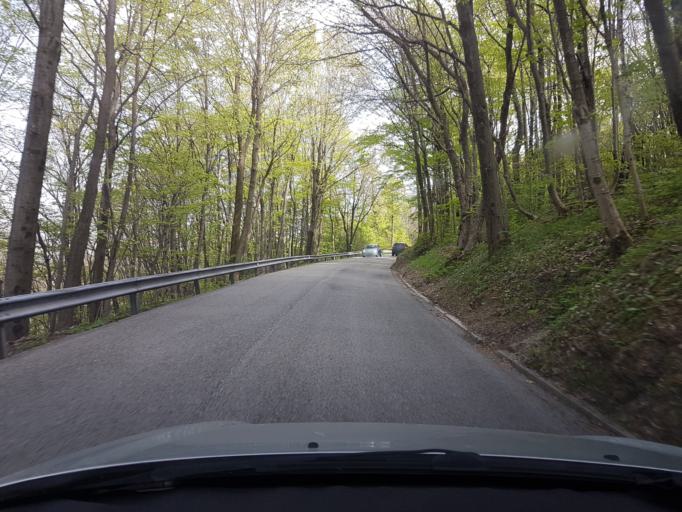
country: IT
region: Friuli Venezia Giulia
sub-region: Provincia di Udine
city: San Leonardo
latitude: 46.0937
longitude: 13.5101
